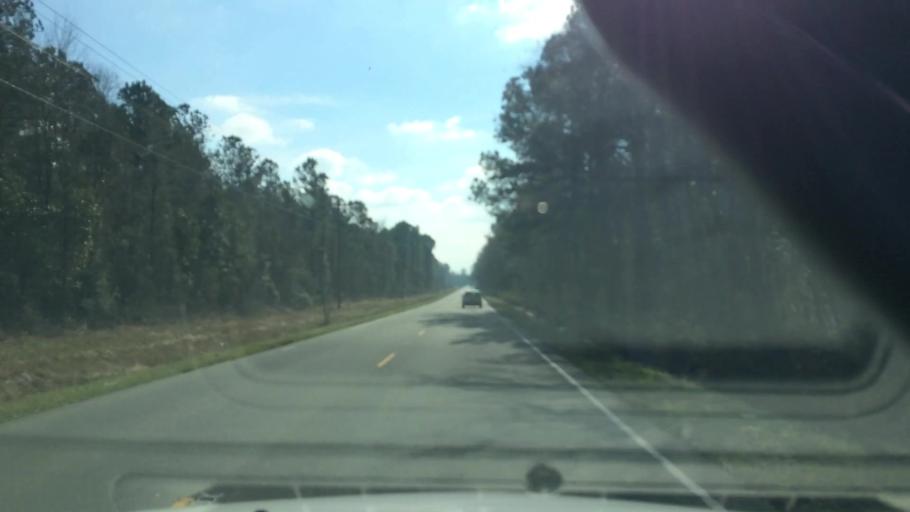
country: US
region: North Carolina
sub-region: Duplin County
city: Beulaville
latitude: 34.8506
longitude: -77.7977
